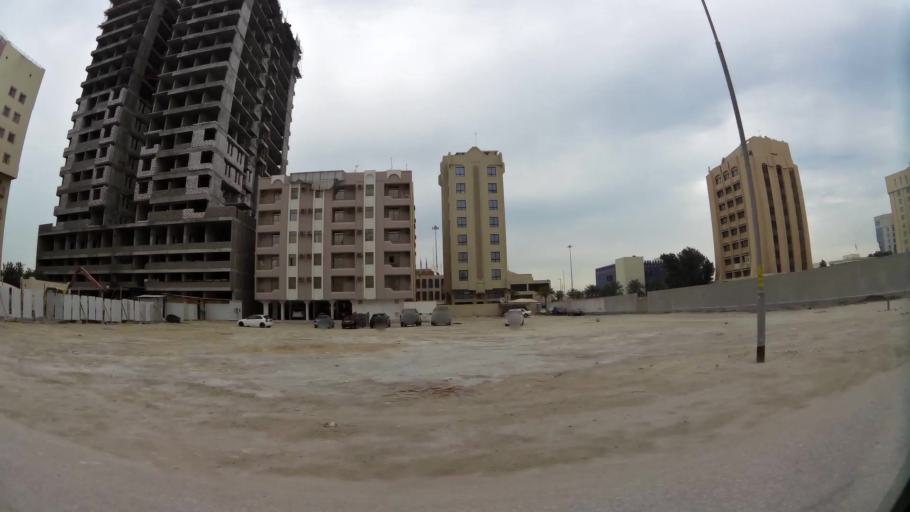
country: BH
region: Manama
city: Manama
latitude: 26.2382
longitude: 50.5940
